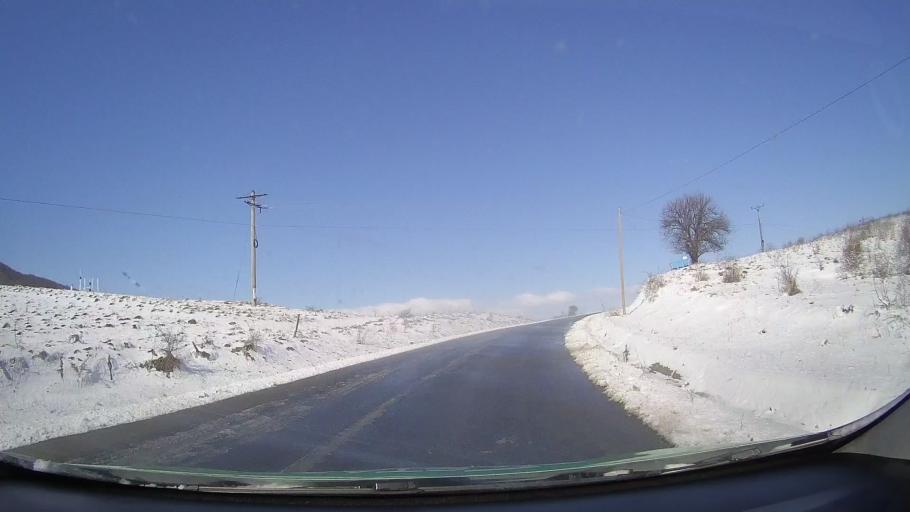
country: RO
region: Sibiu
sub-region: Comuna Avrig
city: Avrig
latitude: 45.7704
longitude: 24.3650
